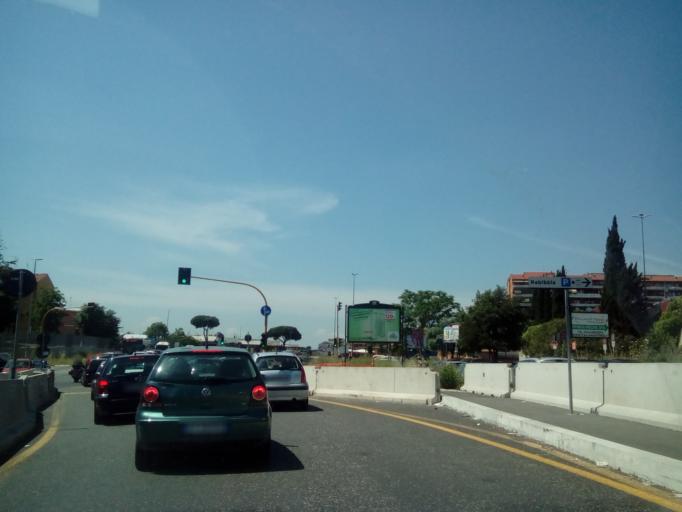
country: IT
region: Latium
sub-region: Citta metropolitana di Roma Capitale
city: Colle Verde
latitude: 41.9271
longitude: 12.5748
